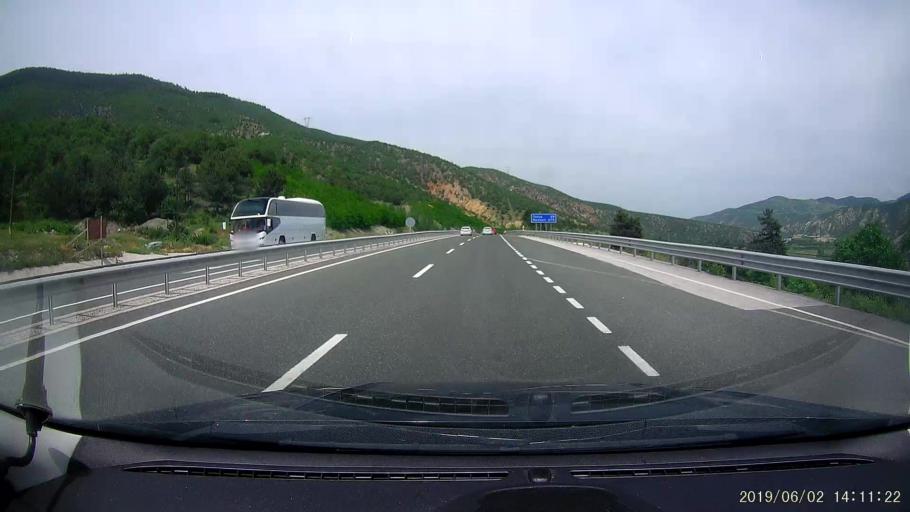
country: TR
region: Cankiri
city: Yaprakli
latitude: 40.9084
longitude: 33.7827
